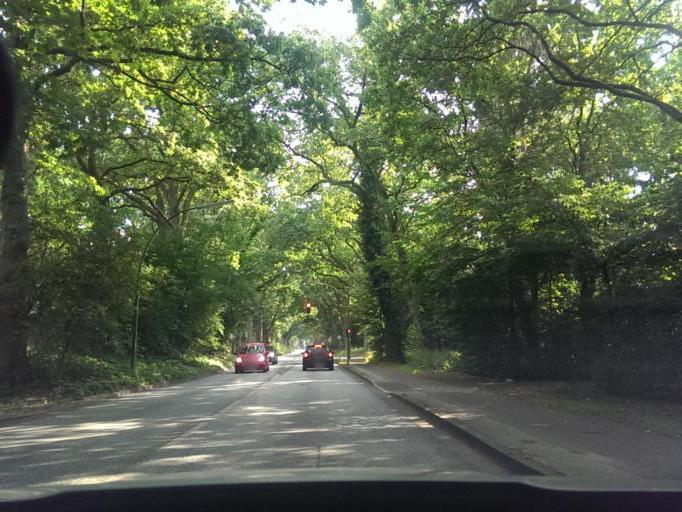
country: DE
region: Hamburg
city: Lemsahl-Mellingstedt
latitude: 53.6835
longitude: 10.0952
